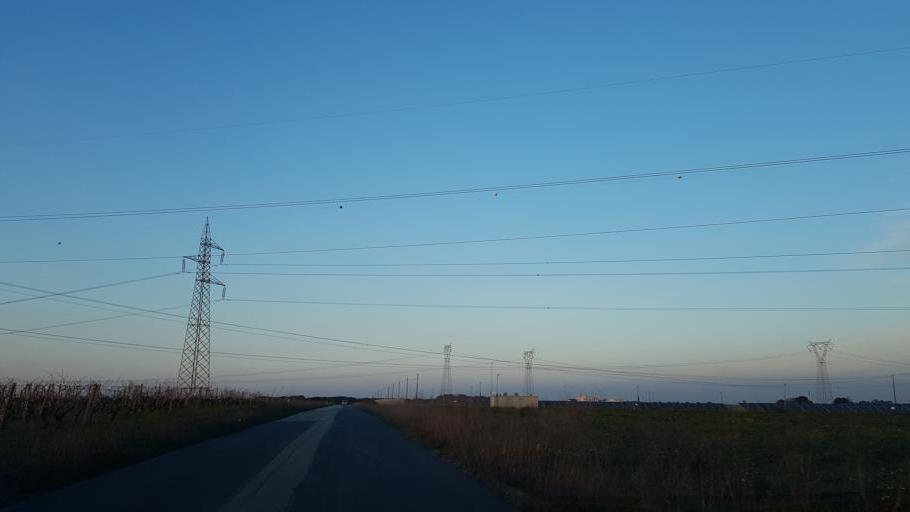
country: IT
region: Apulia
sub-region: Provincia di Brindisi
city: Tuturano
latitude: 40.5549
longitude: 17.9472
